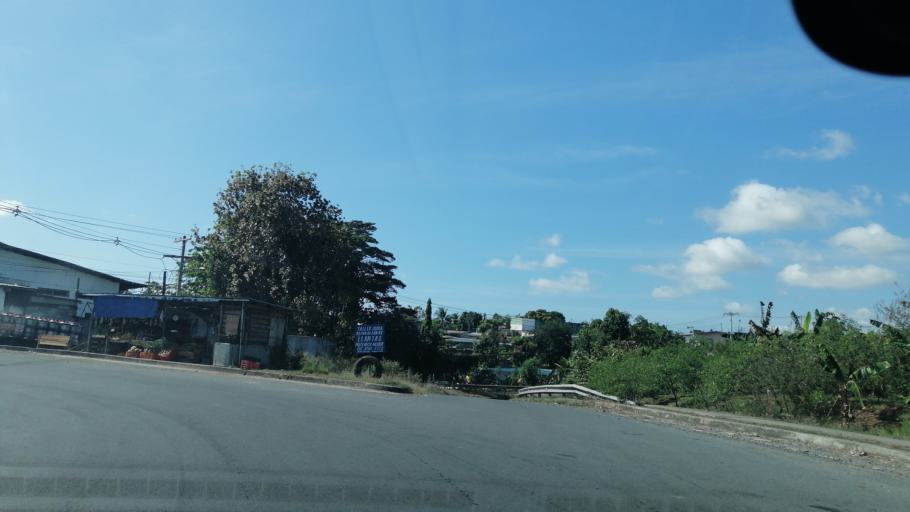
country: PA
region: Panama
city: Tocumen
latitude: 9.0802
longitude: -79.3673
